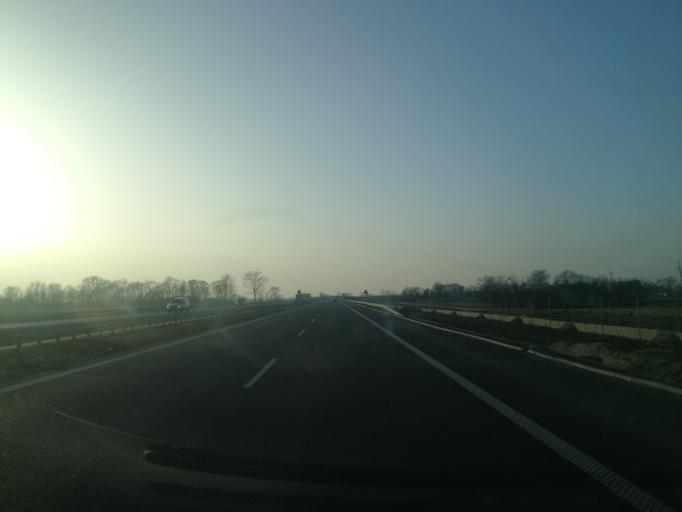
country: PL
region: Pomeranian Voivodeship
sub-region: Powiat nowodworski
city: Nowy Dwor Gdanski
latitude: 54.1732
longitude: 19.2067
